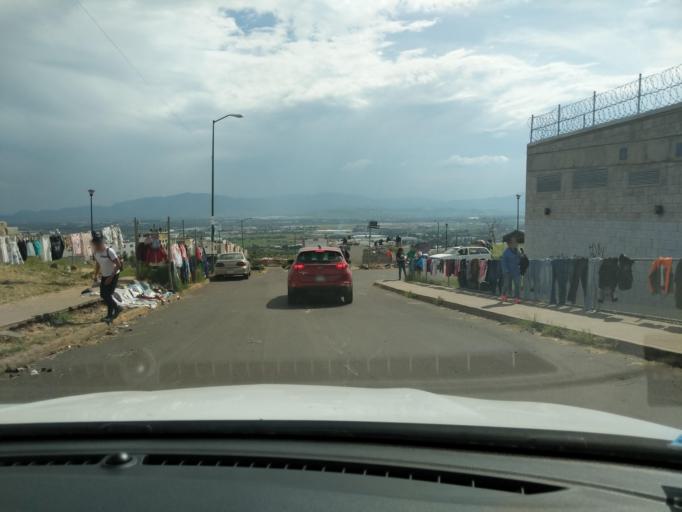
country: MX
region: Jalisco
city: San Jose del Castillo
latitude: 20.5216
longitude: -103.2260
